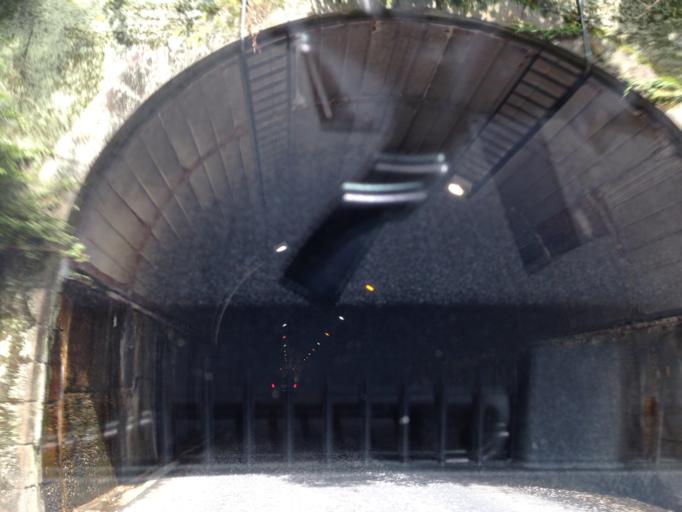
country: JP
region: Shizuoka
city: Numazu
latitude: 35.0251
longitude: 138.9066
